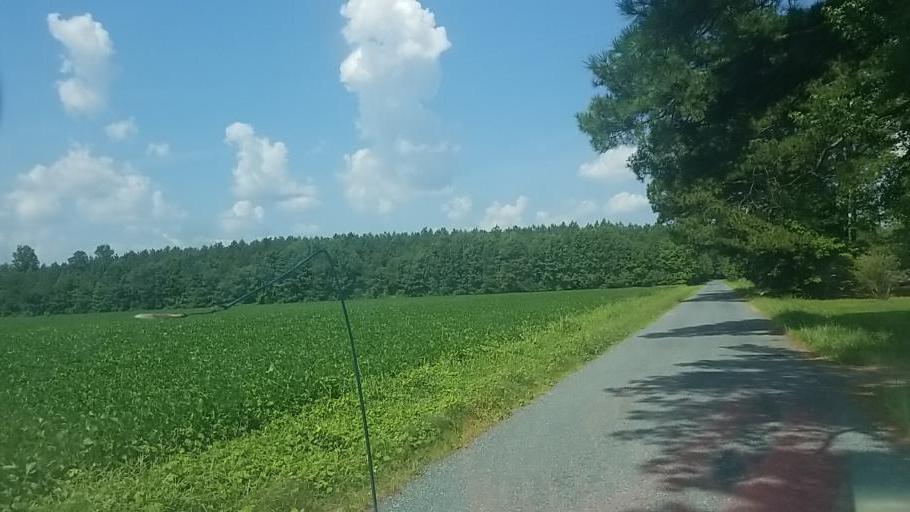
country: US
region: Maryland
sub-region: Worcester County
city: Berlin
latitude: 38.2855
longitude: -75.3048
